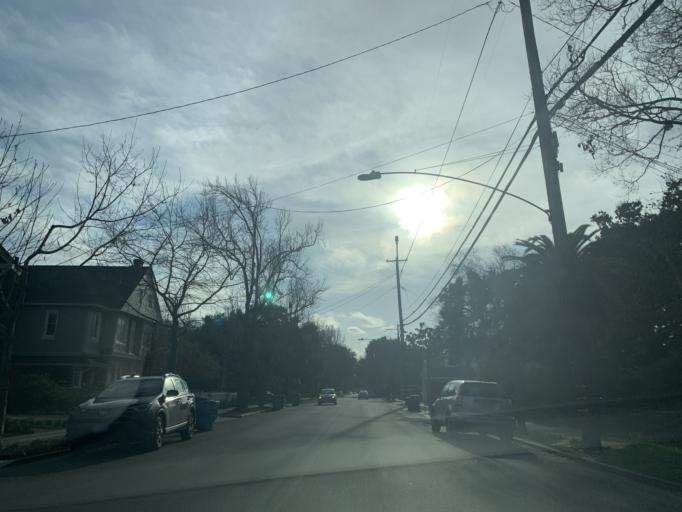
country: US
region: California
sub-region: Santa Clara County
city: Palo Alto
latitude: 37.4444
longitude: -122.1509
